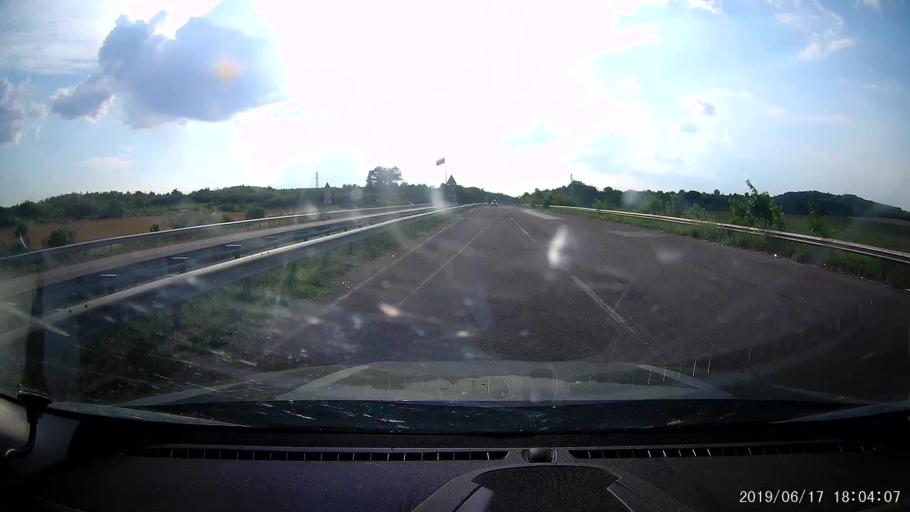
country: BG
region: Khaskovo
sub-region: Obshtina Svilengrad
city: Svilengrad
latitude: 41.7831
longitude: 26.2055
